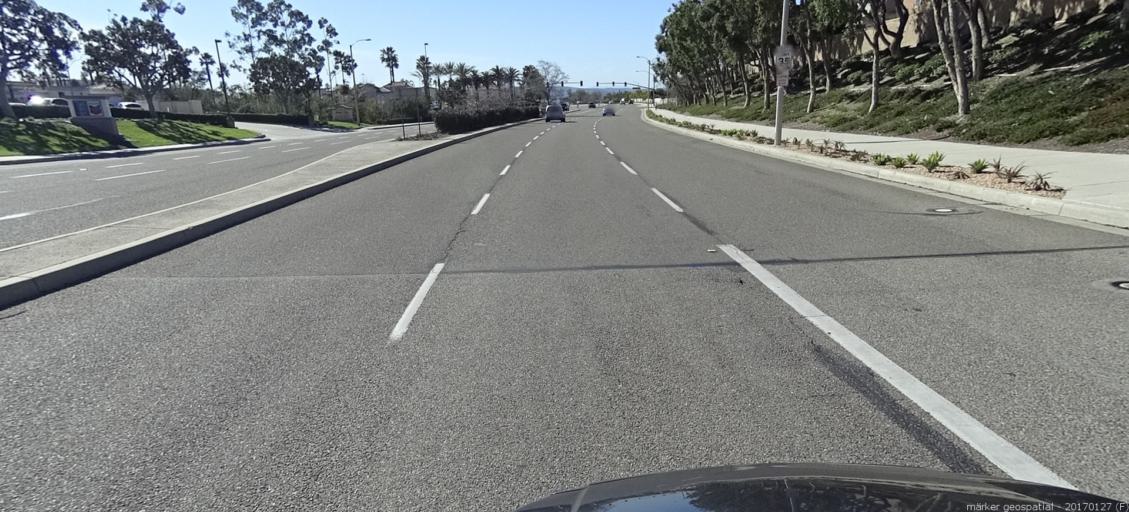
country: US
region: California
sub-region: Orange County
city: Foothill Ranch
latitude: 33.6830
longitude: -117.6670
